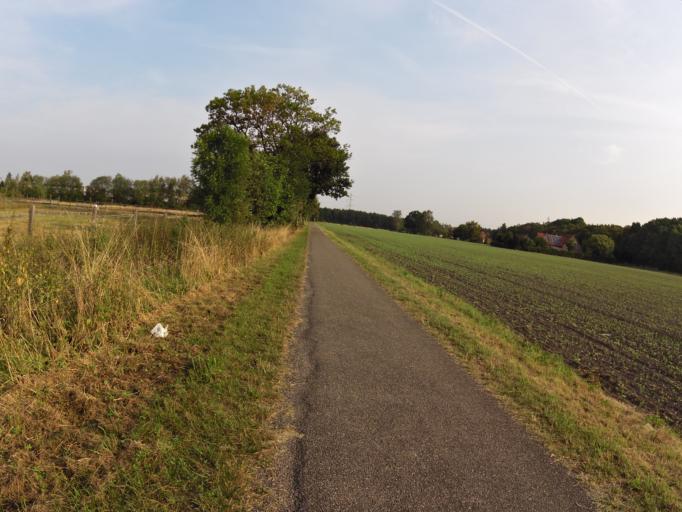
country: DE
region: North Rhine-Westphalia
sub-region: Regierungsbezirk Detmold
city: Petershagen
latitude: 52.3934
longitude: 8.9646
